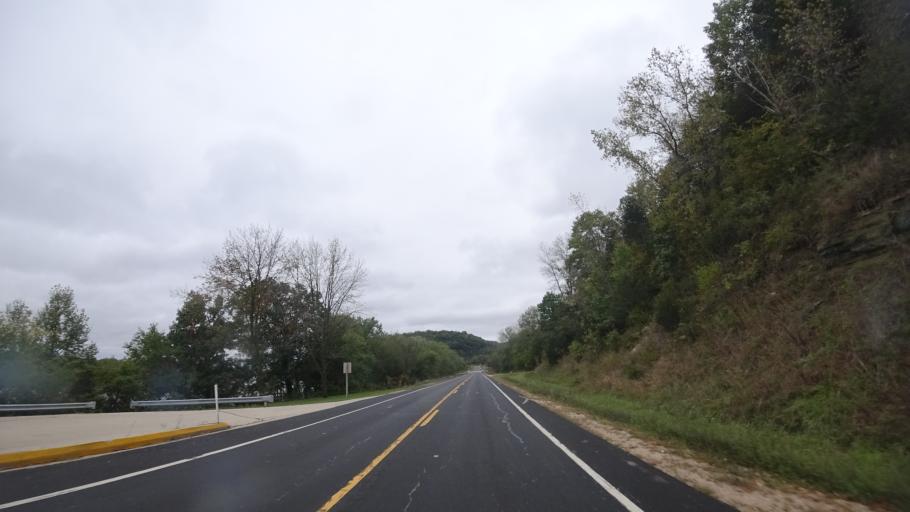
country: US
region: Wisconsin
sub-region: Grant County
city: Boscobel
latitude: 43.1709
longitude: -90.6965
